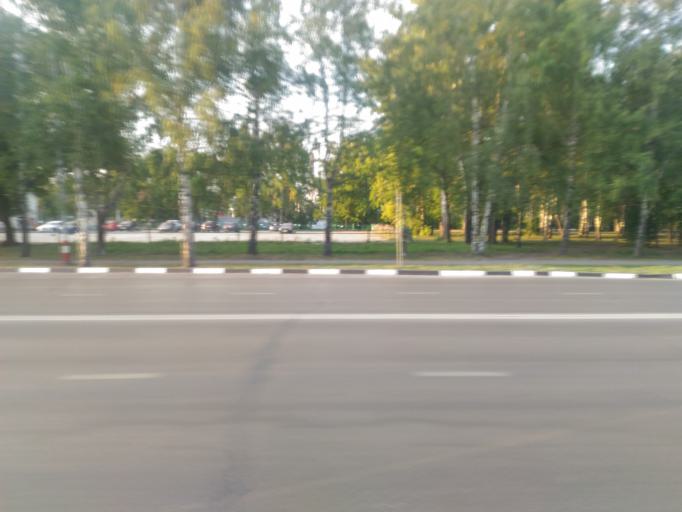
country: RU
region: Ulyanovsk
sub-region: Ulyanovskiy Rayon
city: Ulyanovsk
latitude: 54.3080
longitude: 48.3370
